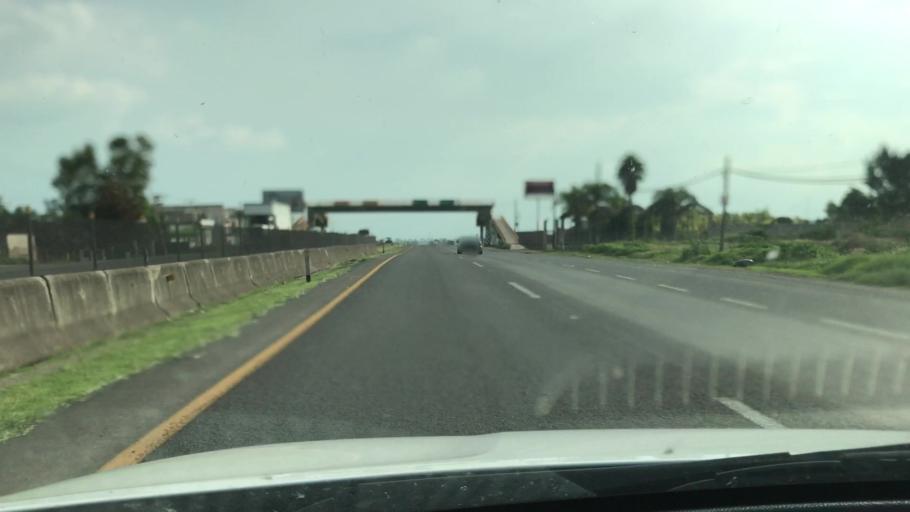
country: MX
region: Guanajuato
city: Penjamo
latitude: 20.4172
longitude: -101.7274
